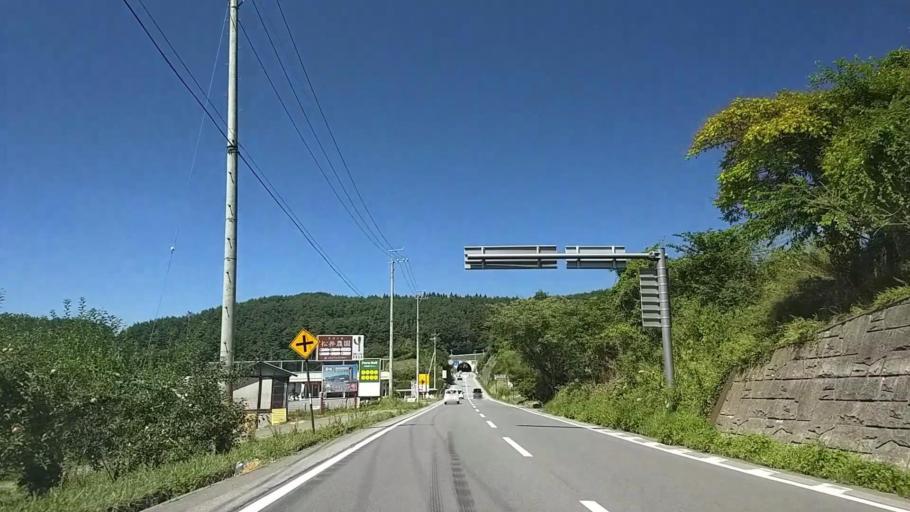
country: JP
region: Nagano
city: Komoro
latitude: 36.3398
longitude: 138.4466
